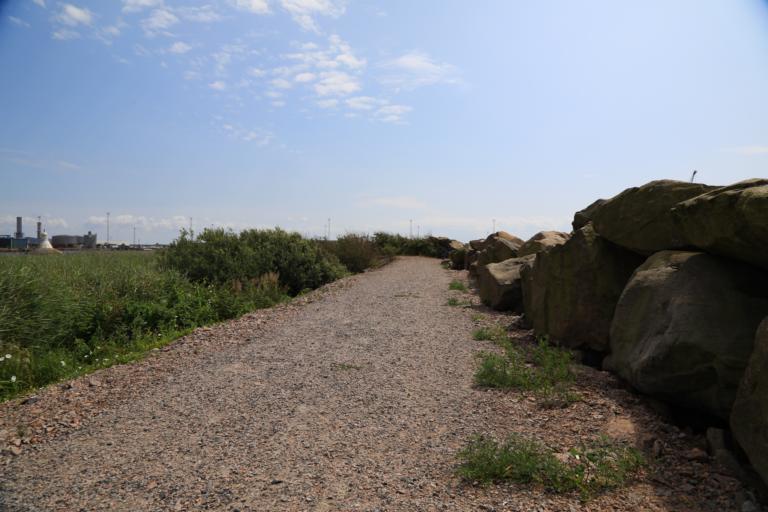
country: SE
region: Halland
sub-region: Halmstads Kommun
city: Halmstad
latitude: 56.6554
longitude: 12.8464
